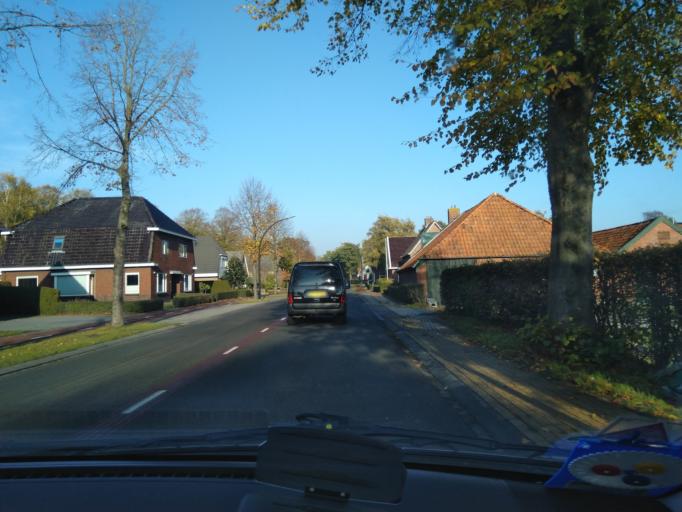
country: NL
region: Drenthe
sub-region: Gemeente Tynaarlo
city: Zuidlaren
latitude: 53.1145
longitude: 6.7165
